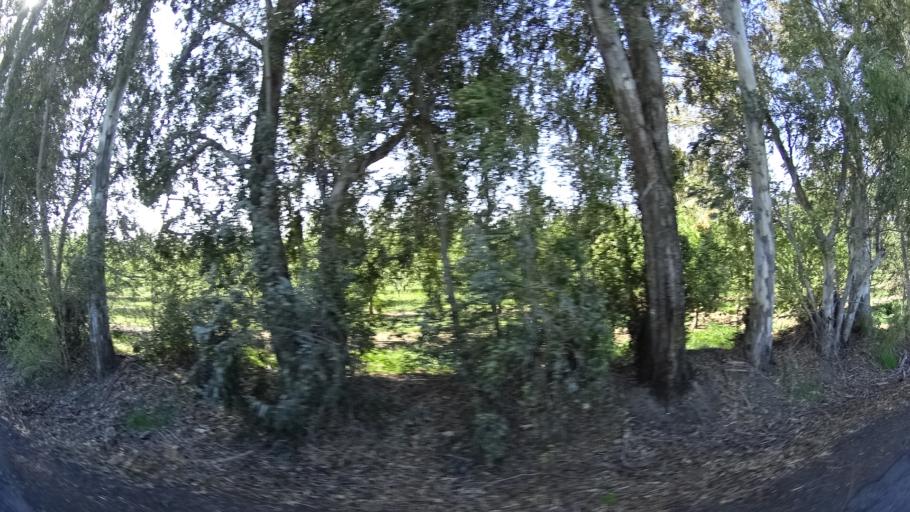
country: US
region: California
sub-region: Glenn County
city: Hamilton City
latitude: 39.7969
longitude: -122.0965
